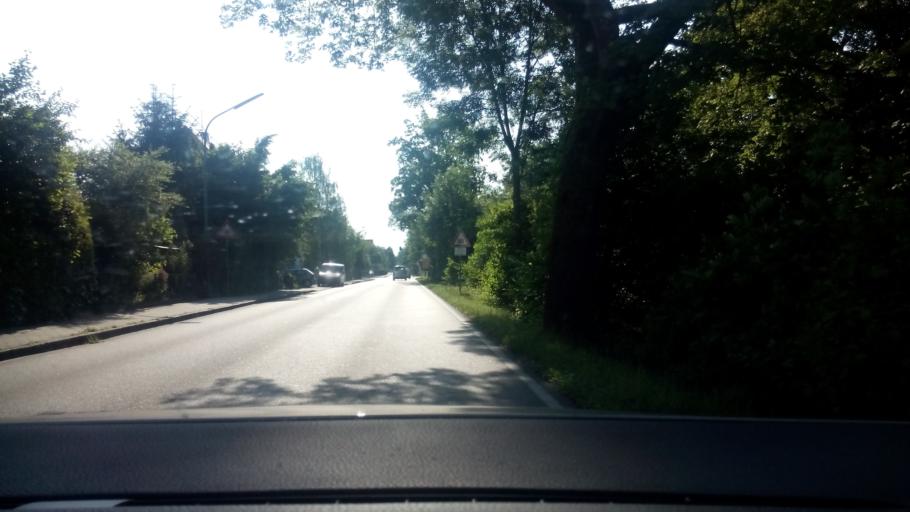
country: DE
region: Bavaria
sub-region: Upper Bavaria
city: Oberschleissheim
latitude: 48.2510
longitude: 11.5499
